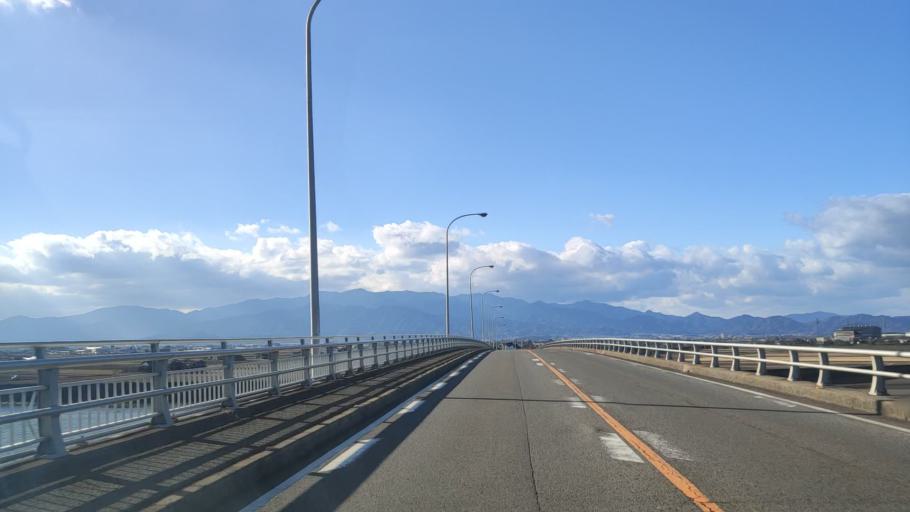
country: JP
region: Ehime
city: Saijo
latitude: 33.9156
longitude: 133.1341
